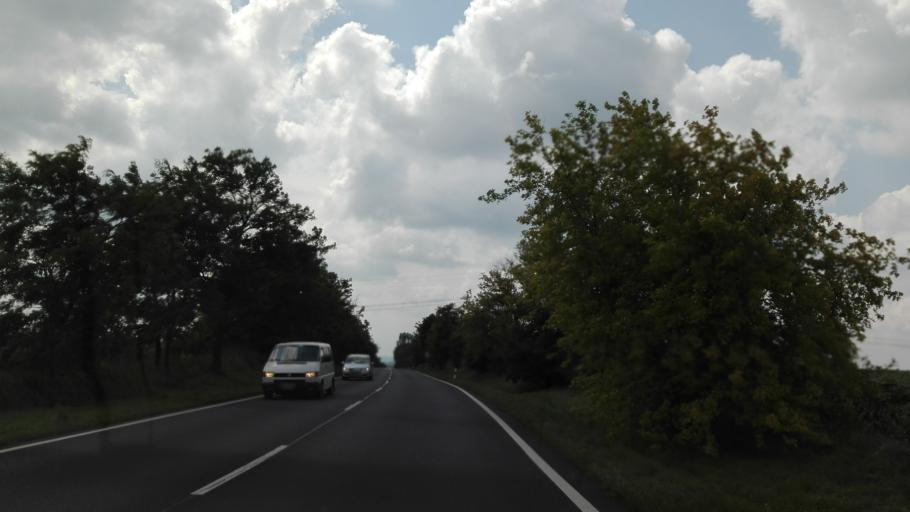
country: HU
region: Fejer
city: Alap
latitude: 46.8033
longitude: 18.7562
